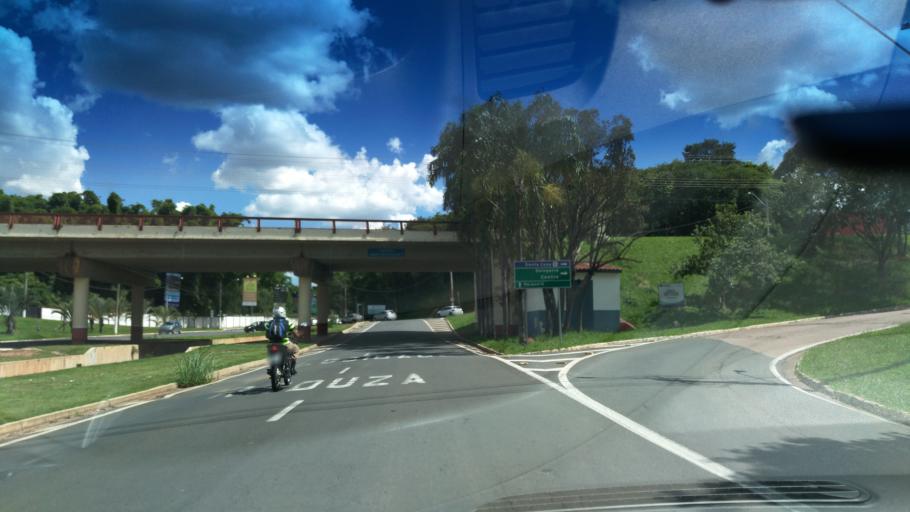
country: BR
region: Sao Paulo
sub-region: Valinhos
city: Valinhos
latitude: -22.9648
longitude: -47.0075
